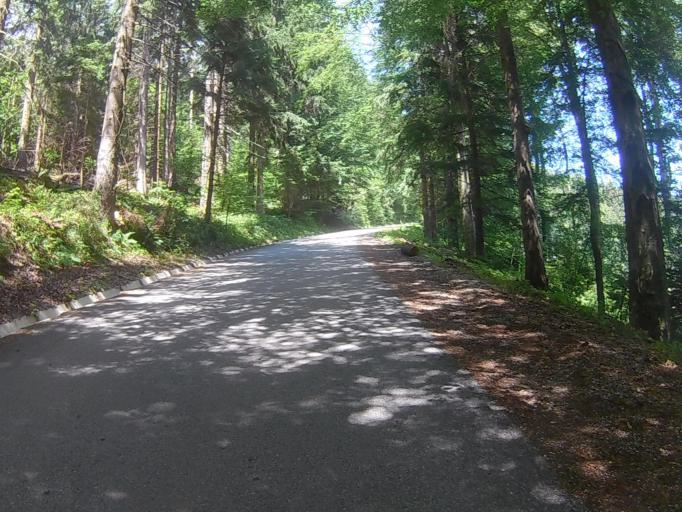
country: SI
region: Maribor
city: Pekre
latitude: 46.4973
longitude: 15.5664
